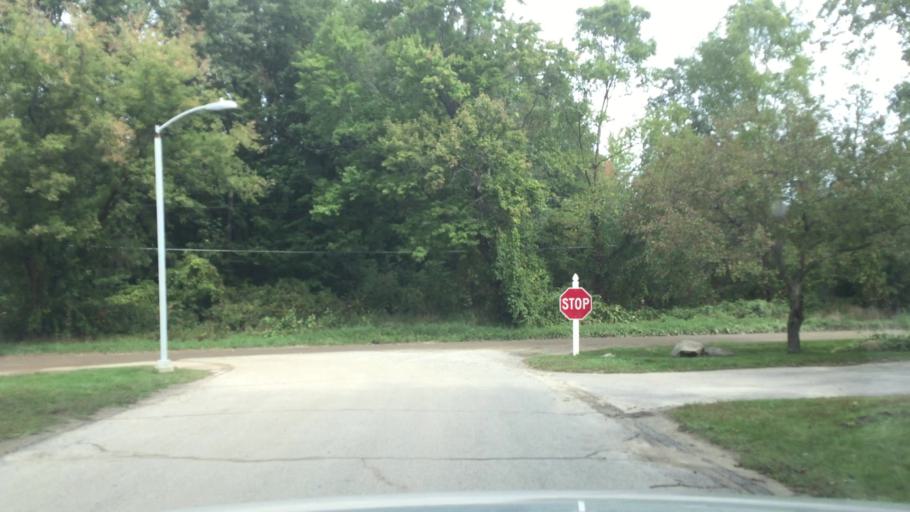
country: US
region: Michigan
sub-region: Oakland County
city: Holly
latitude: 42.8143
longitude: -83.6228
